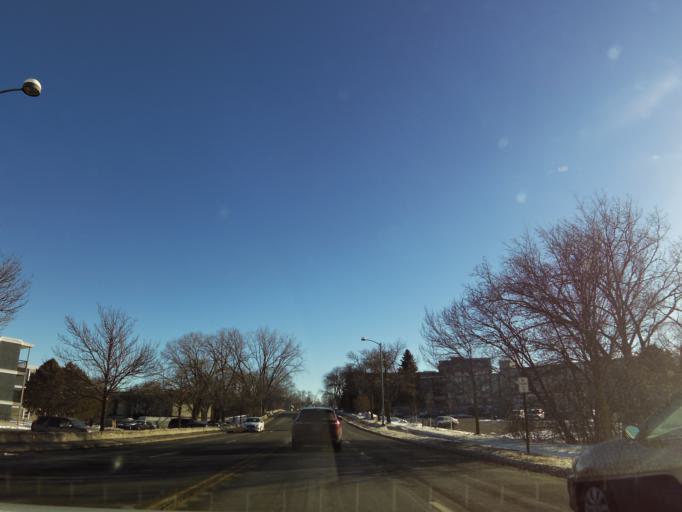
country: US
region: Minnesota
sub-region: Hennepin County
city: Saint Louis Park
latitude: 44.9365
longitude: -93.3391
